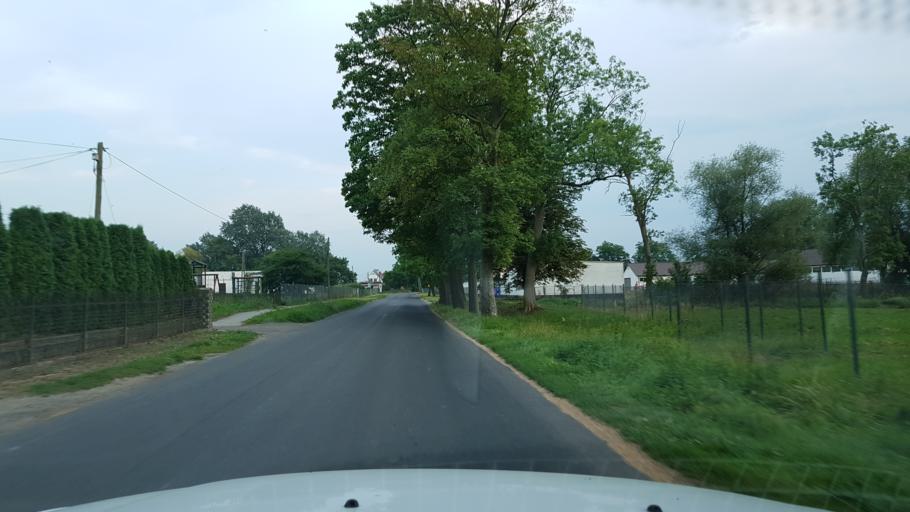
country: PL
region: West Pomeranian Voivodeship
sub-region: Powiat koszalinski
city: Mielno
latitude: 54.2271
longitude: 16.0236
